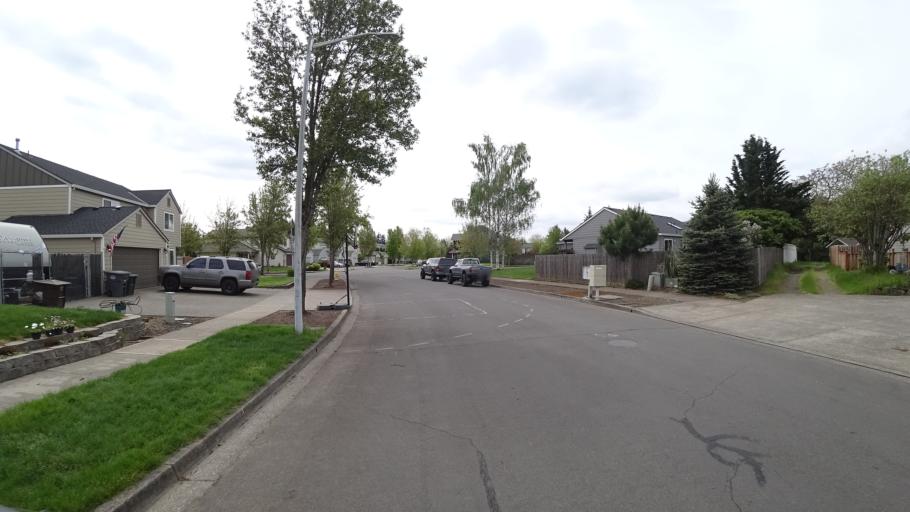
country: US
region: Oregon
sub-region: Washington County
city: Hillsboro
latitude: 45.5454
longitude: -122.9945
